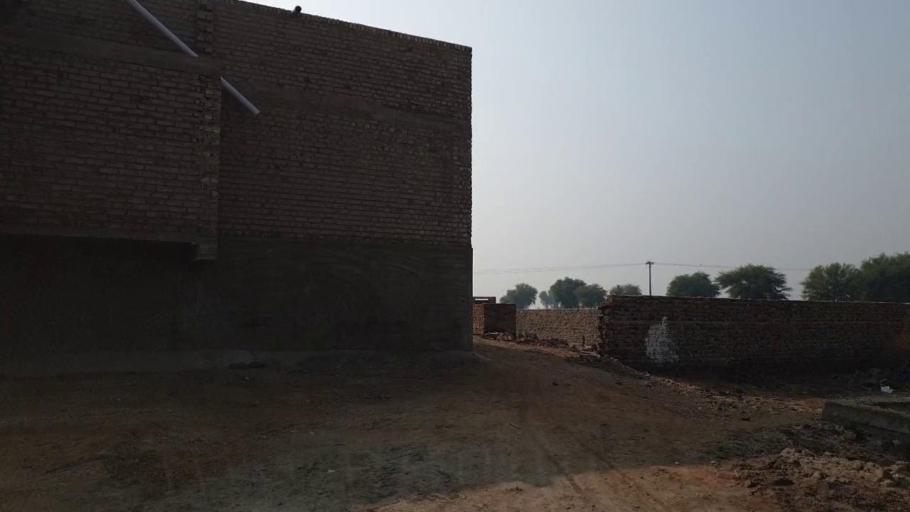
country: PK
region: Sindh
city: Sehwan
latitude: 26.4332
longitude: 67.8294
